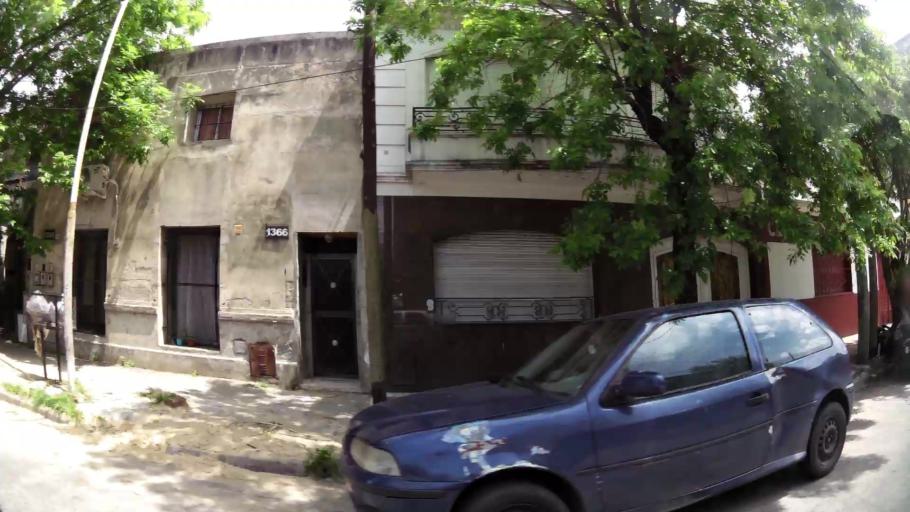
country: AR
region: Buenos Aires
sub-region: Partido de Avellaneda
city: Avellaneda
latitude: -34.6678
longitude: -58.3973
